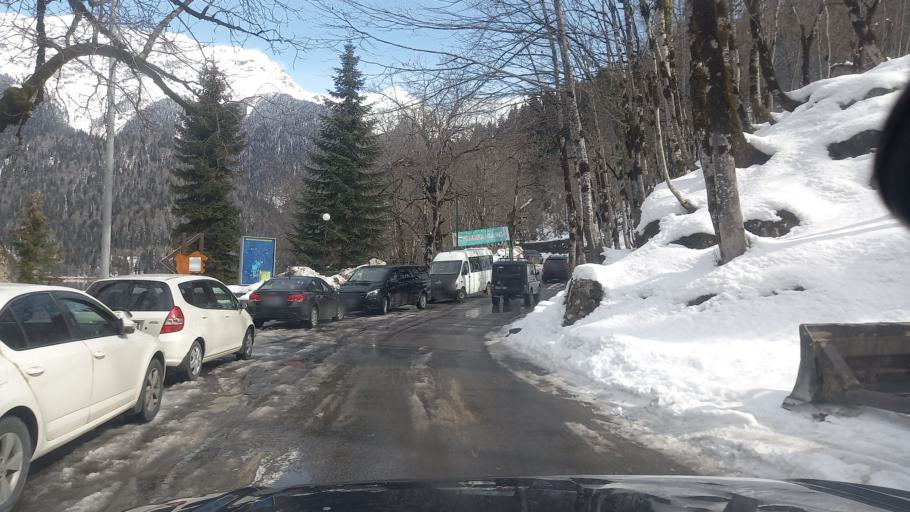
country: GE
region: Abkhazia
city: Gagra
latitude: 43.4713
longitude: 40.5339
